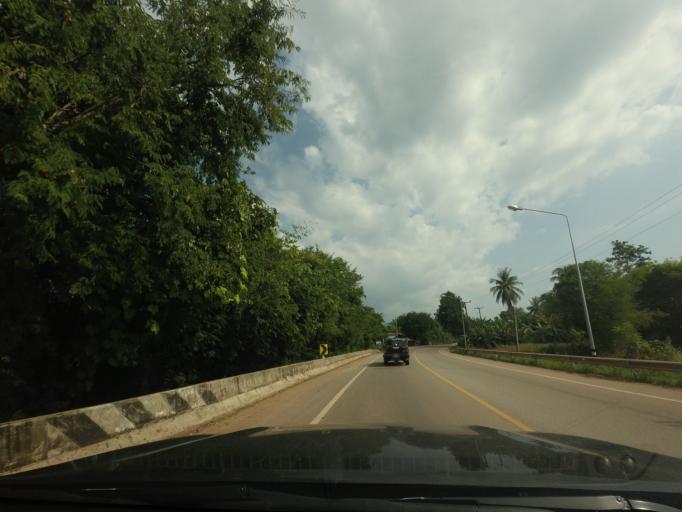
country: TH
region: Phitsanulok
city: Nakhon Thai
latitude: 17.0367
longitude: 100.9137
